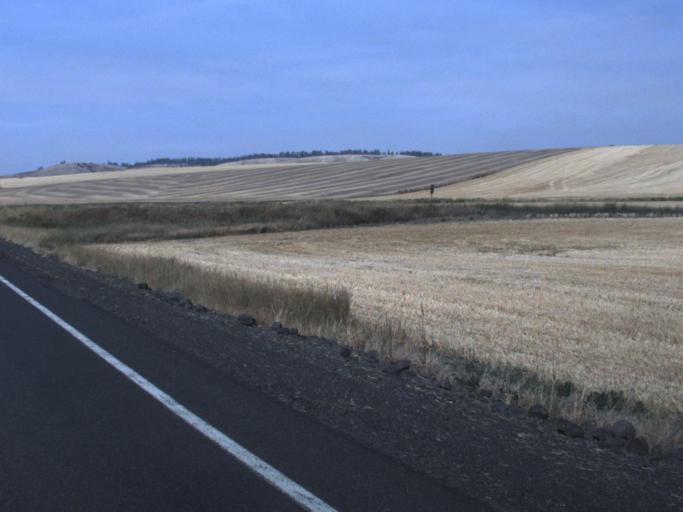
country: US
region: Idaho
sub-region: Benewah County
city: Plummer
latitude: 47.3171
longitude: -117.1725
